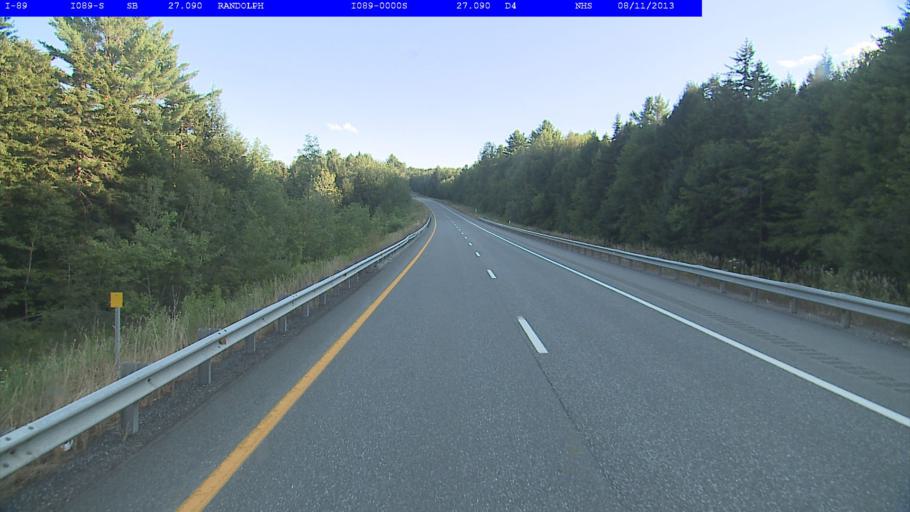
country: US
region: Vermont
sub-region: Orange County
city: Randolph
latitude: 43.8909
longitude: -72.6176
